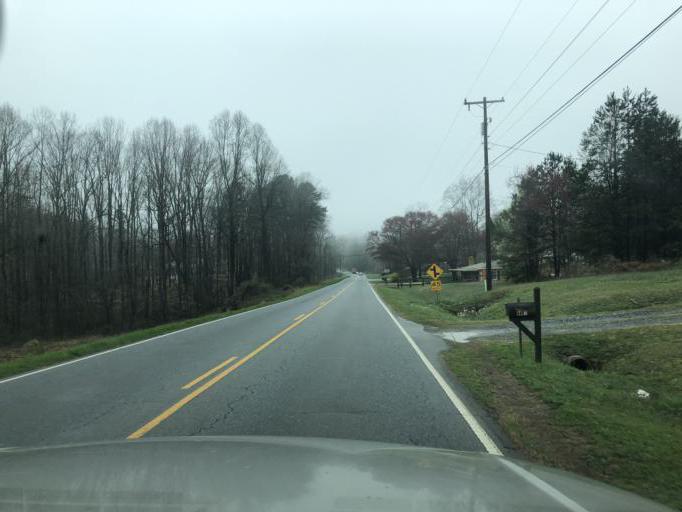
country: US
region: North Carolina
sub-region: Cleveland County
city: Shelby
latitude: 35.3292
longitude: -81.4686
